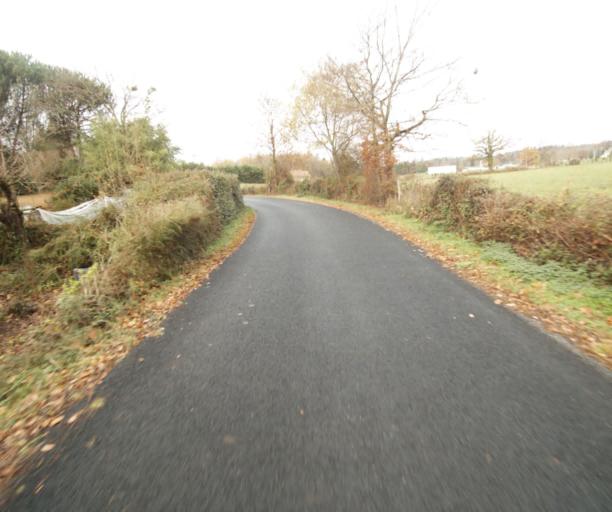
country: FR
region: Limousin
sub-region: Departement de la Correze
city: Saint-Mexant
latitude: 45.2684
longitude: 1.6352
